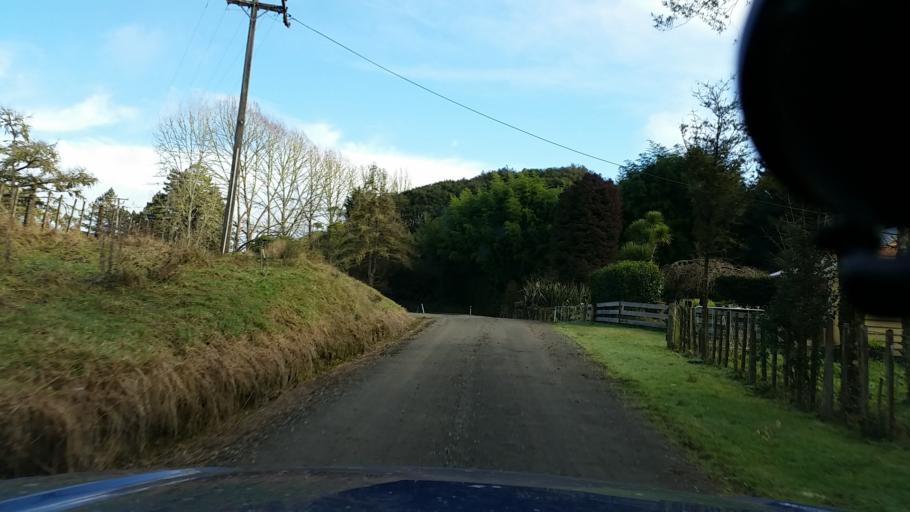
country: NZ
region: Taranaki
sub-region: New Plymouth District
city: Waitara
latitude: -39.0339
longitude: 174.7978
